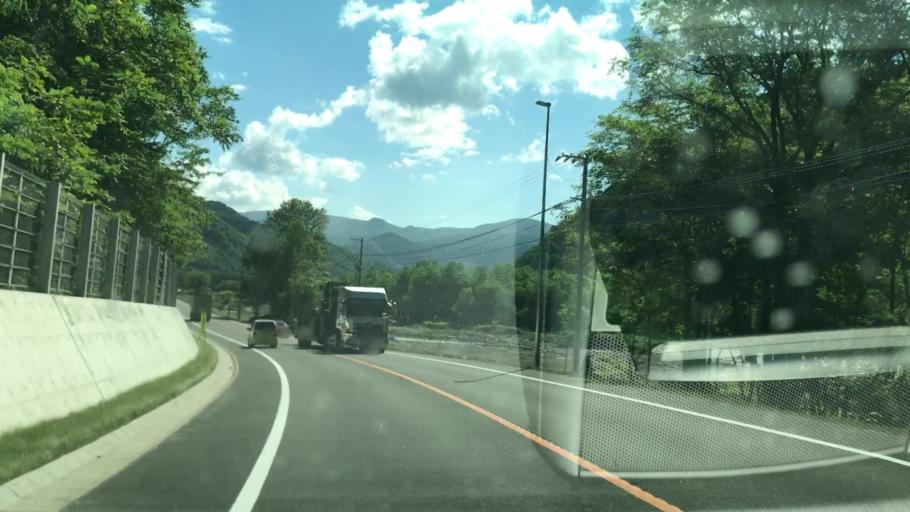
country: JP
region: Hokkaido
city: Shimo-furano
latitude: 42.9048
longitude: 142.5678
